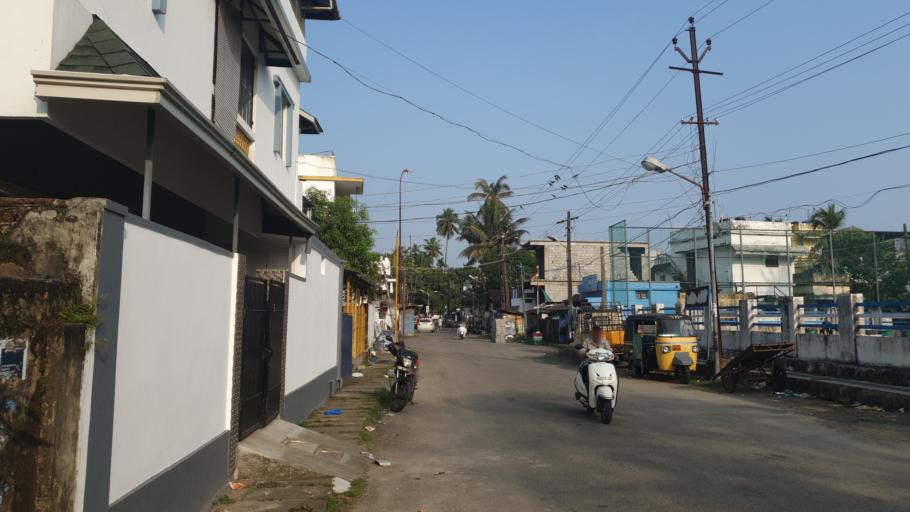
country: IN
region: Kerala
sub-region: Ernakulam
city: Cochin
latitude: 9.9610
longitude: 76.2518
